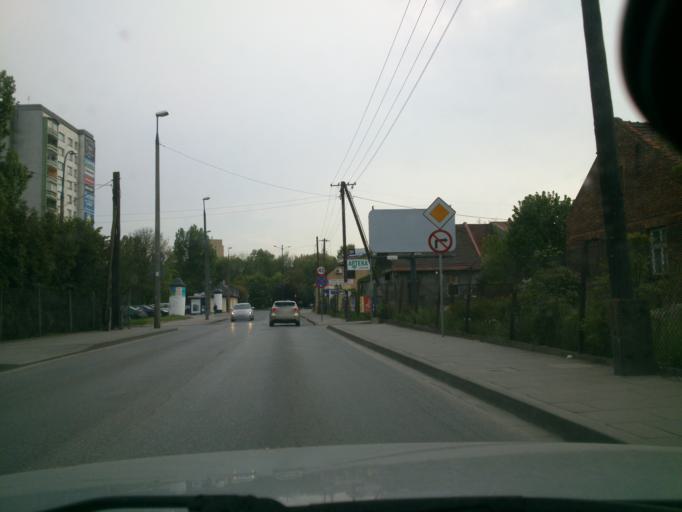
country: PL
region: Lesser Poland Voivodeship
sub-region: Krakow
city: Krakow
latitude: 50.0915
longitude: 19.9443
